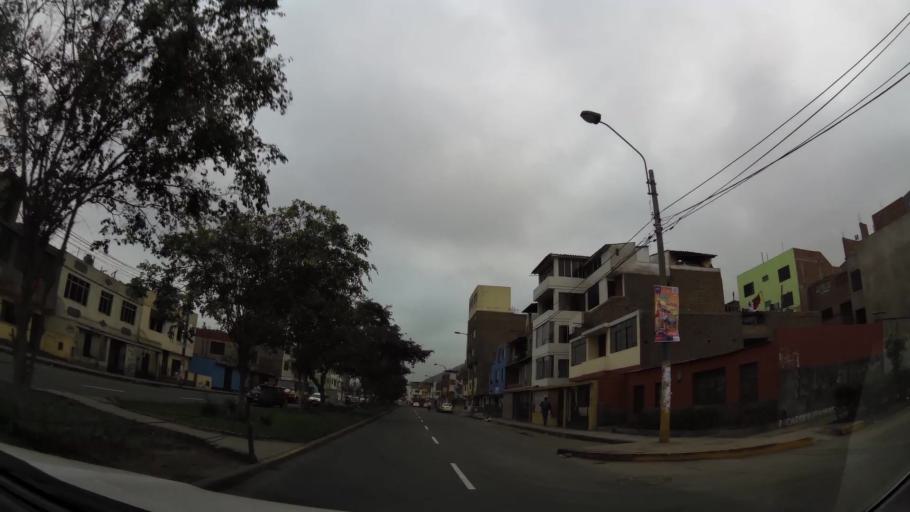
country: PE
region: Lima
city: Lima
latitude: -12.0212
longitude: -77.0127
